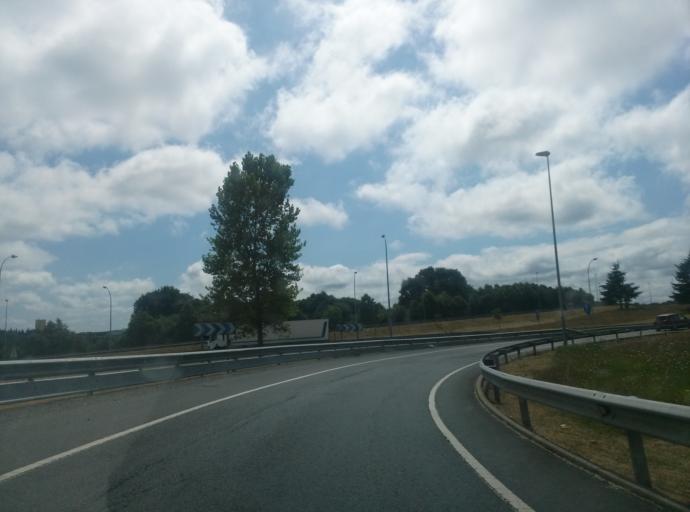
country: ES
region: Galicia
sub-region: Provincia de Lugo
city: Lugo
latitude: 43.0579
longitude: -7.5577
